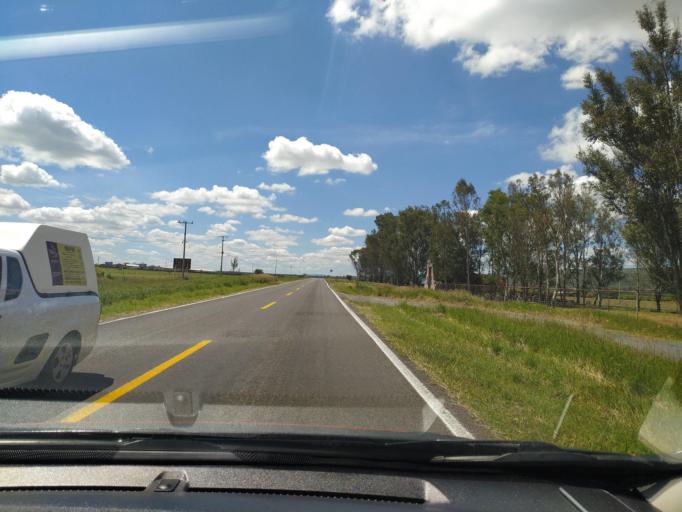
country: MX
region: Jalisco
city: San Miguel el Alto
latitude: 21.0183
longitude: -102.4634
